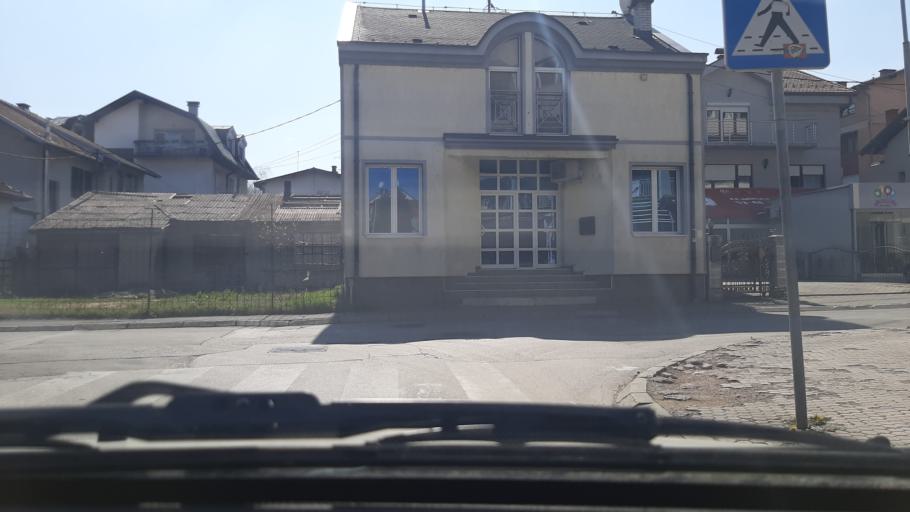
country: BA
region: Republika Srpska
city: Hiseti
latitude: 44.7679
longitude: 17.1826
